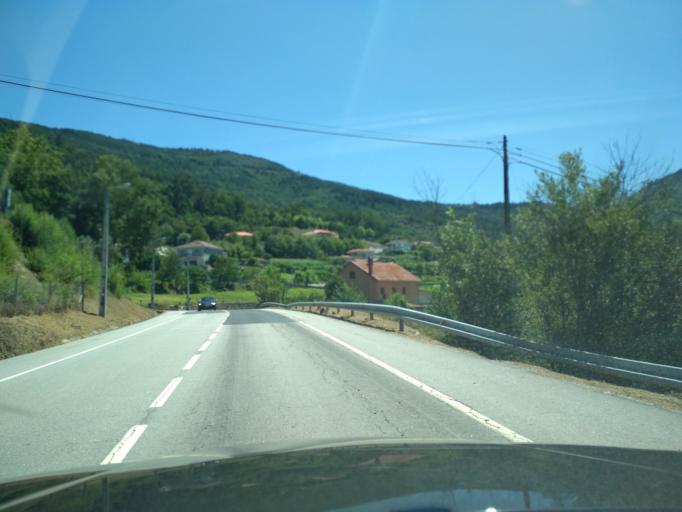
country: PT
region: Vila Real
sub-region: Ribeira de Pena
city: Sobreira
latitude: 41.5247
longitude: -7.7863
